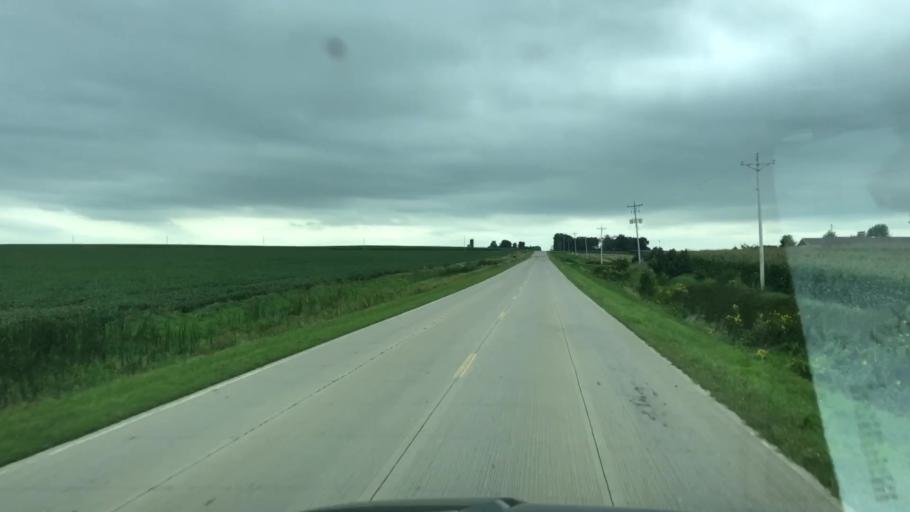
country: US
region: Iowa
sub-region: Sioux County
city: Alton
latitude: 43.1036
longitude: -95.9785
